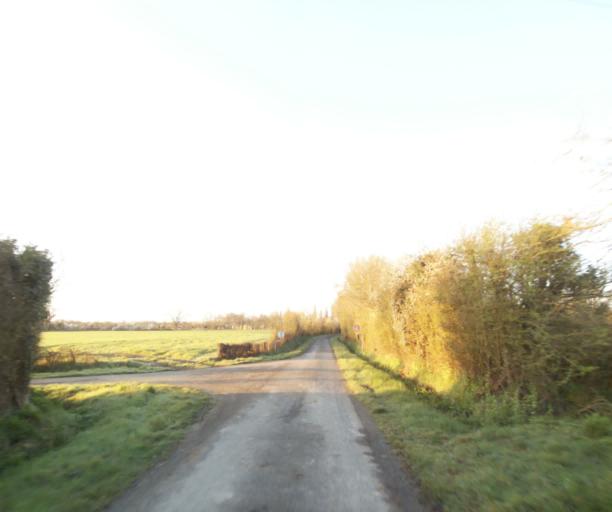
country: FR
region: Pays de la Loire
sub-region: Departement de la Loire-Atlantique
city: Bouvron
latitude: 47.4265
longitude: -1.8829
